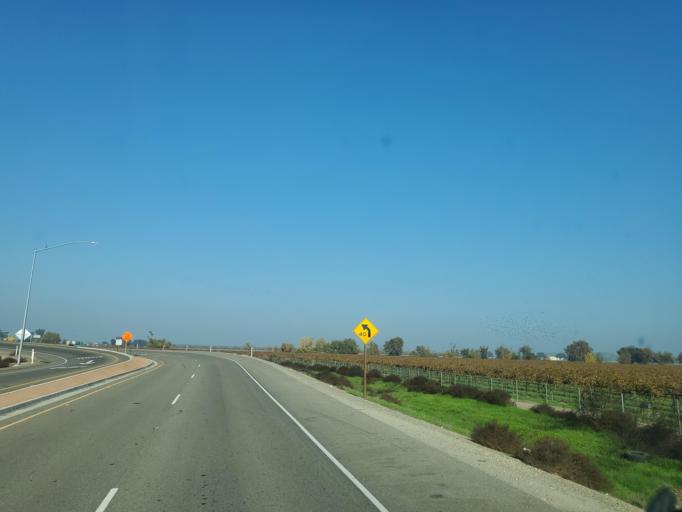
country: US
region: California
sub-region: San Joaquin County
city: French Camp
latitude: 37.8607
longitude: -121.2170
